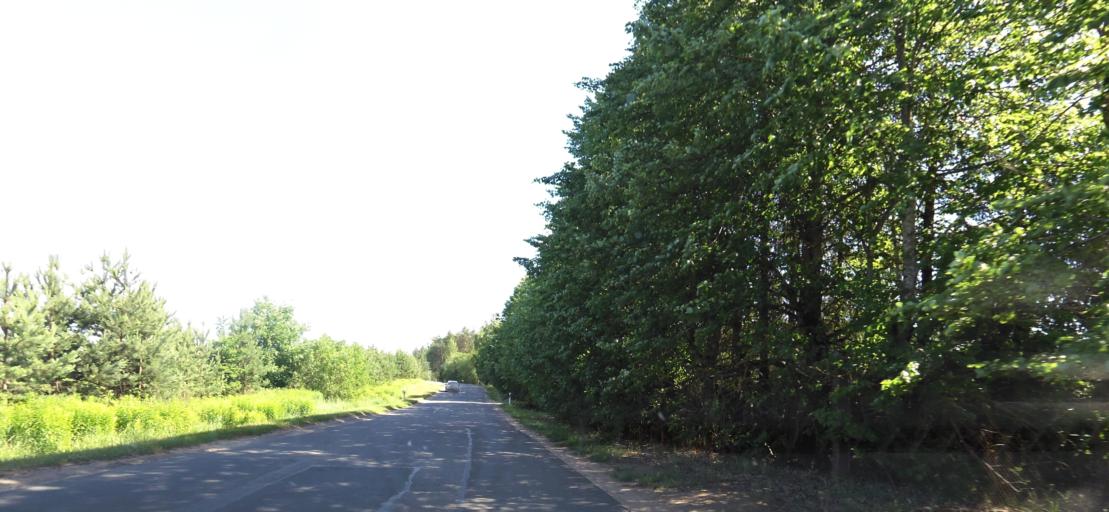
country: LT
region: Vilnius County
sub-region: Vilnius
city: Fabijoniskes
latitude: 54.8045
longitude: 25.3287
